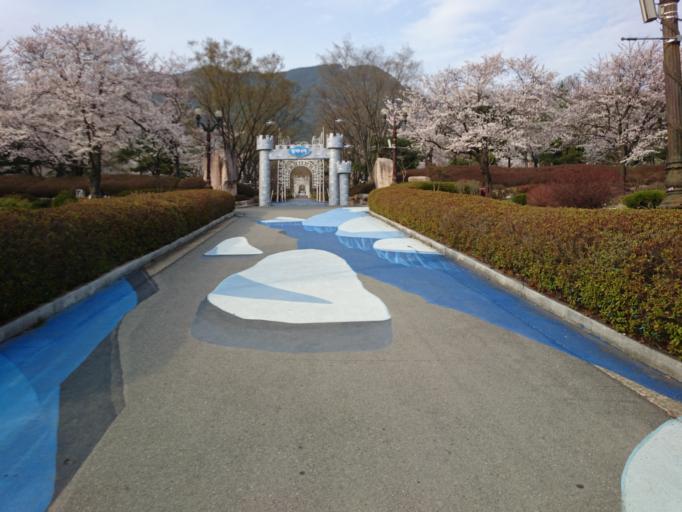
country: KR
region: Gyeongsangnam-do
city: Changnyeong
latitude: 35.4405
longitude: 128.5936
